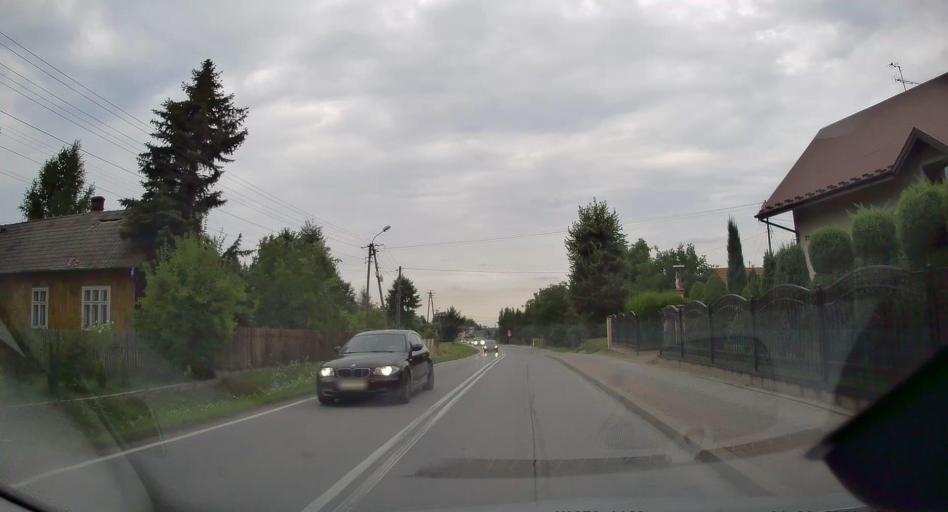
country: PL
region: Lesser Poland Voivodeship
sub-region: Powiat tarnowski
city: Wojnicz
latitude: 49.9907
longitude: 20.8399
